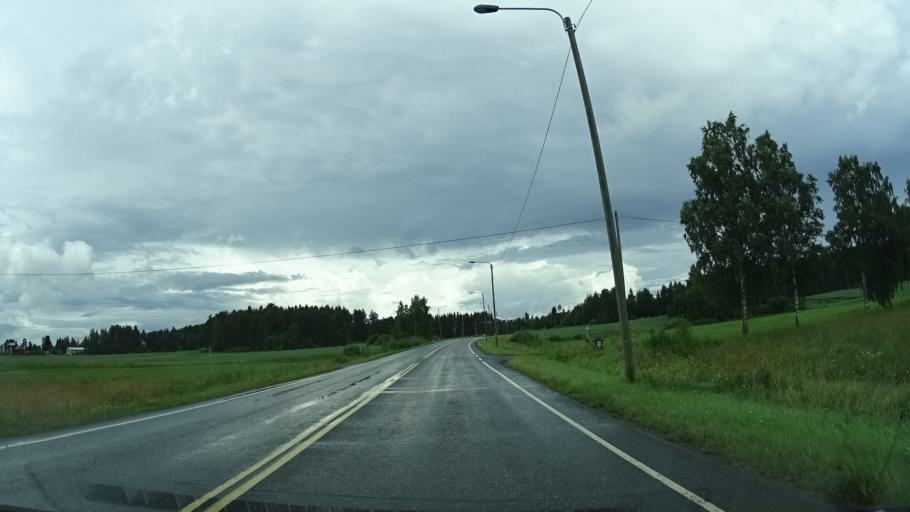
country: FI
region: Pirkanmaa
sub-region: Etelae-Pirkanmaa
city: Valkeakoski
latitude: 61.1659
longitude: 24.0383
